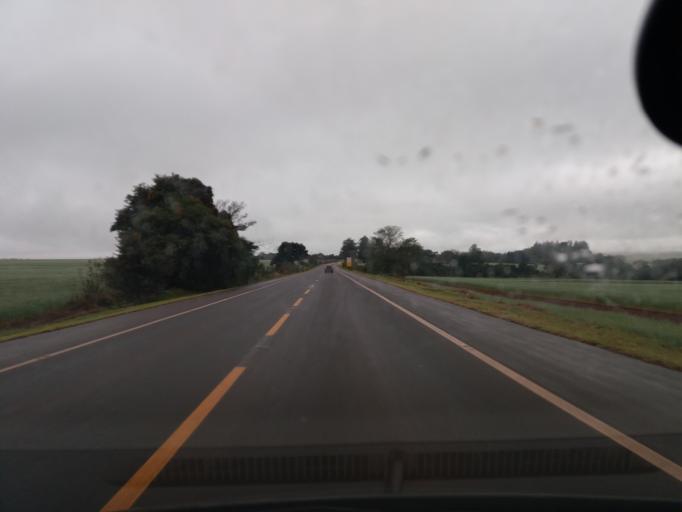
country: BR
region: Parana
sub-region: Moreira Sales
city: Moreira Sales
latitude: -24.3353
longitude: -52.6929
